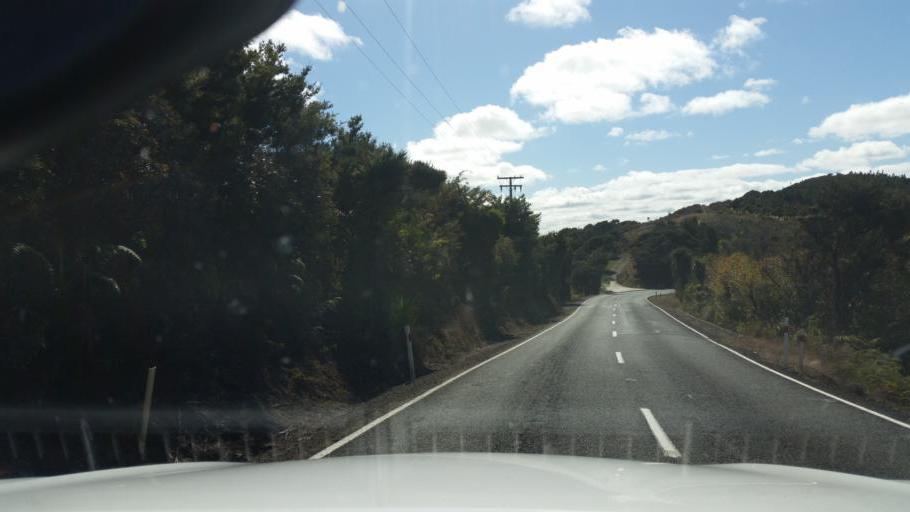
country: NZ
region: Auckland
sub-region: Auckland
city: Wellsford
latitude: -36.1900
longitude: 174.1565
